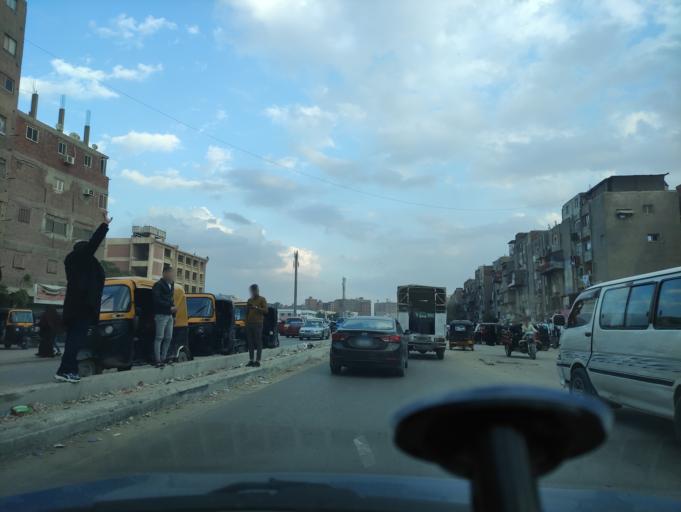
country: EG
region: Muhafazat al Qalyubiyah
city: Al Khankah
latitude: 30.1368
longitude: 31.3504
